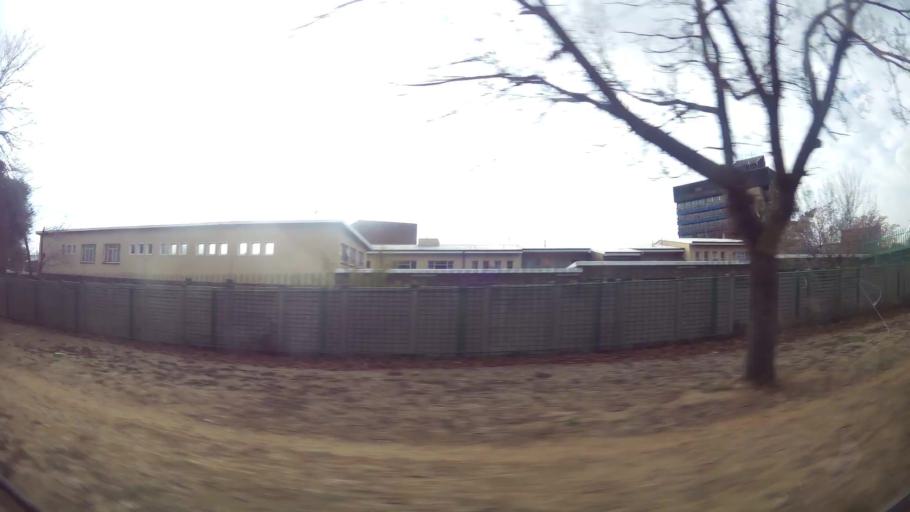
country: ZA
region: Orange Free State
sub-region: Fezile Dabi District Municipality
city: Sasolburg
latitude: -26.8191
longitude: 27.8272
